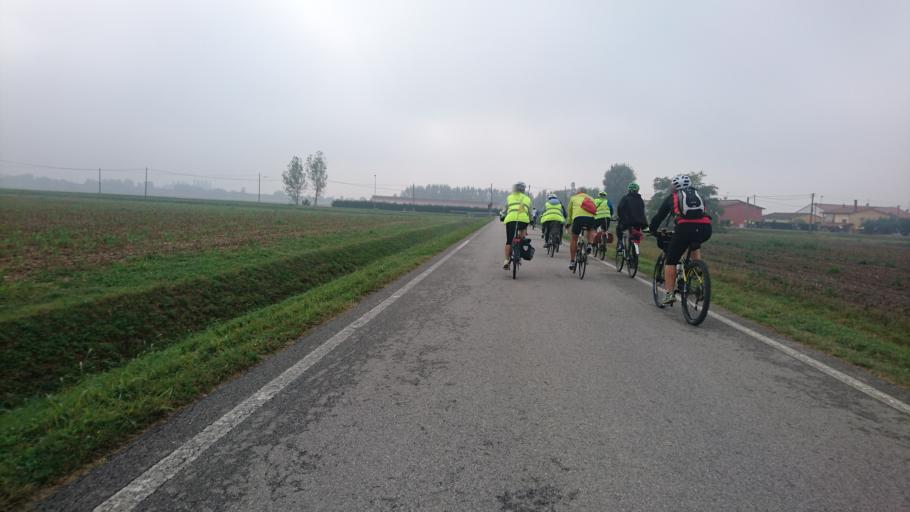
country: IT
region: Veneto
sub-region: Provincia di Padova
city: Stanghella
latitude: 45.1575
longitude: 11.7881
